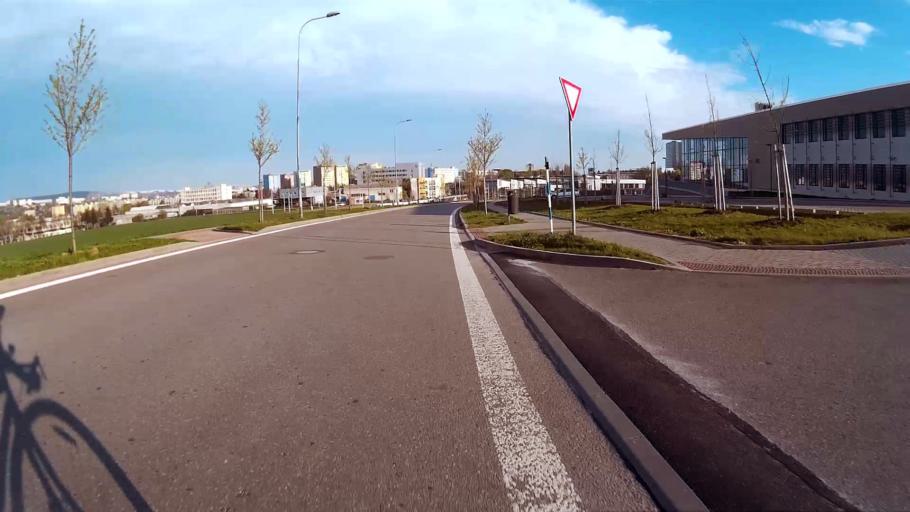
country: CZ
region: South Moravian
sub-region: Mesto Brno
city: Mokra Hora
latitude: 49.2340
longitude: 16.5748
